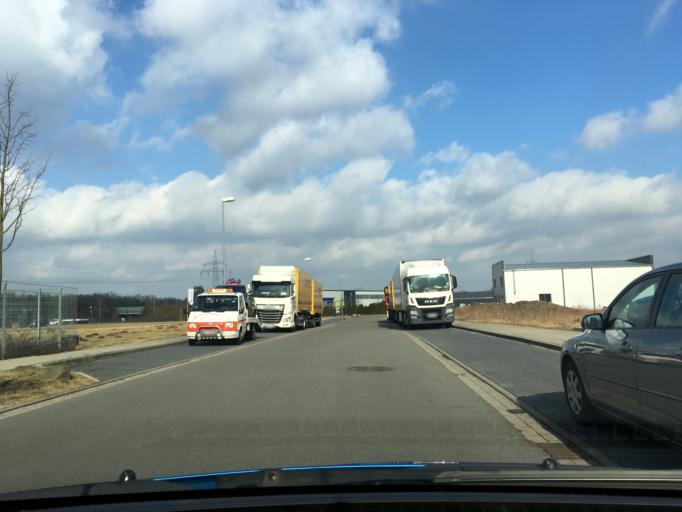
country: DE
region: Lower Saxony
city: Winsen
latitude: 53.3342
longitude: 10.2168
